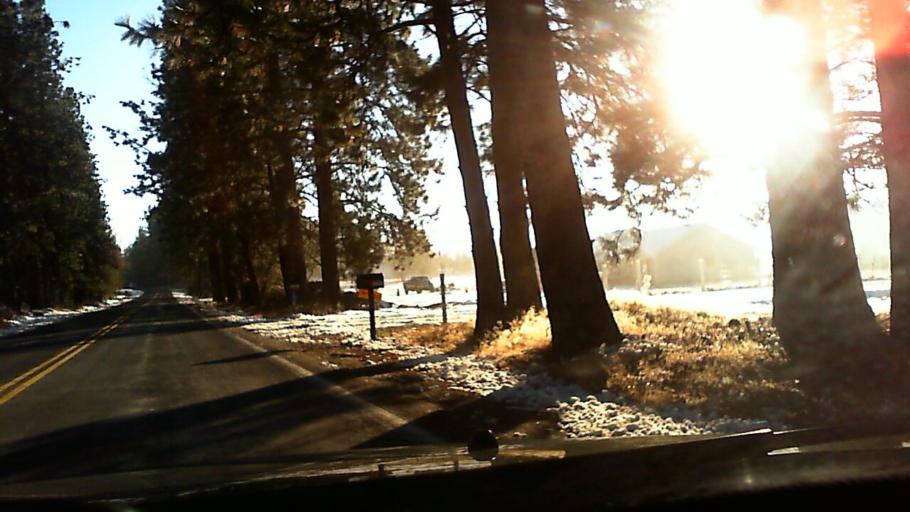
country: US
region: Washington
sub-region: Spokane County
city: Trentwood
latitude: 47.7279
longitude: -117.2131
